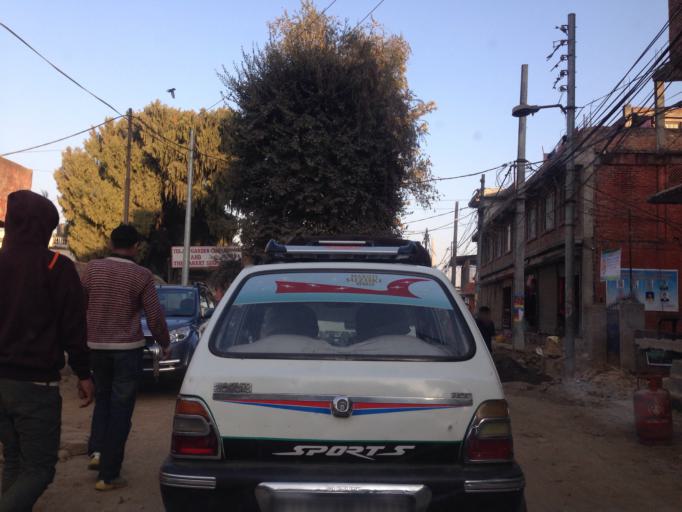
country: NP
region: Central Region
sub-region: Bagmati Zone
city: Kathmandu
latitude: 27.7144
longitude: 85.2940
